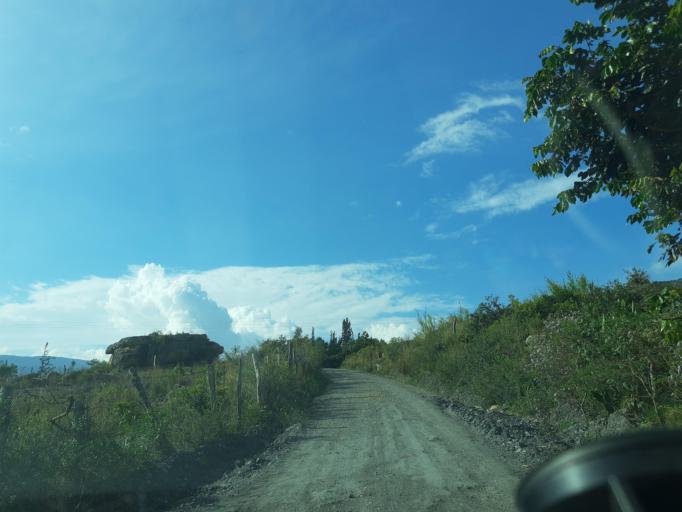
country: CO
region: Boyaca
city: Villa de Leiva
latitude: 5.6650
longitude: -73.5620
